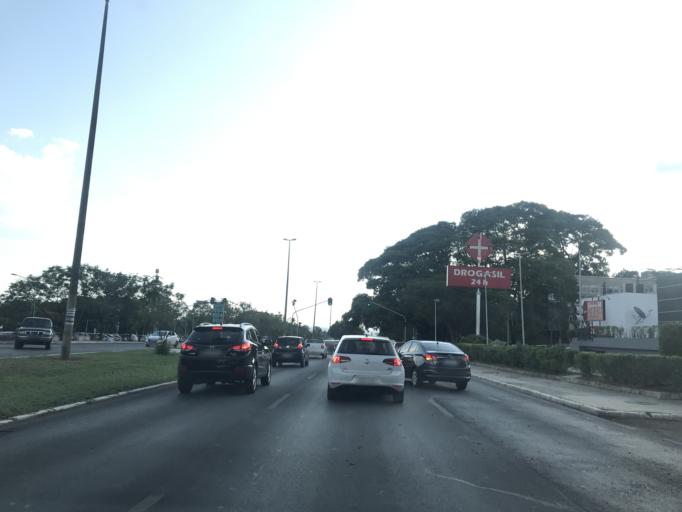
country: BR
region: Federal District
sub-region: Brasilia
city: Brasilia
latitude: -15.8149
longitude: -47.8886
